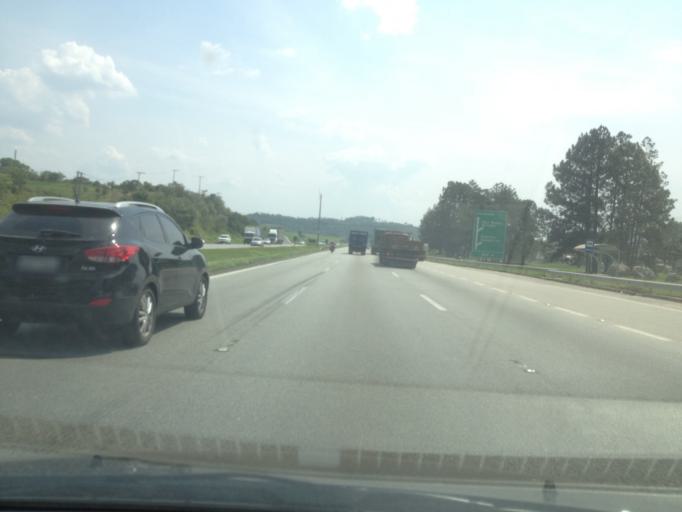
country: BR
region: Sao Paulo
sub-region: Sao Roque
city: Sao Roque
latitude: -23.4370
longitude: -47.0980
